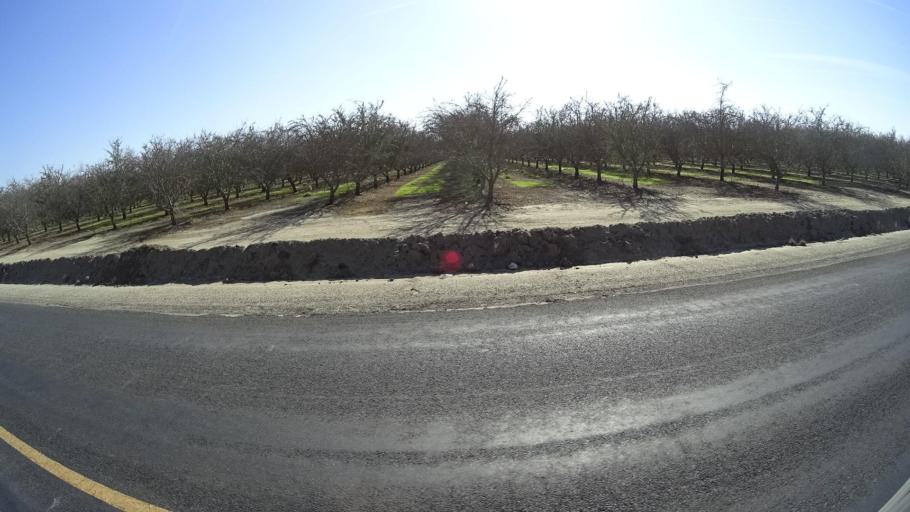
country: US
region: California
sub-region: Kern County
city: Wasco
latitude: 35.6452
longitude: -119.2992
